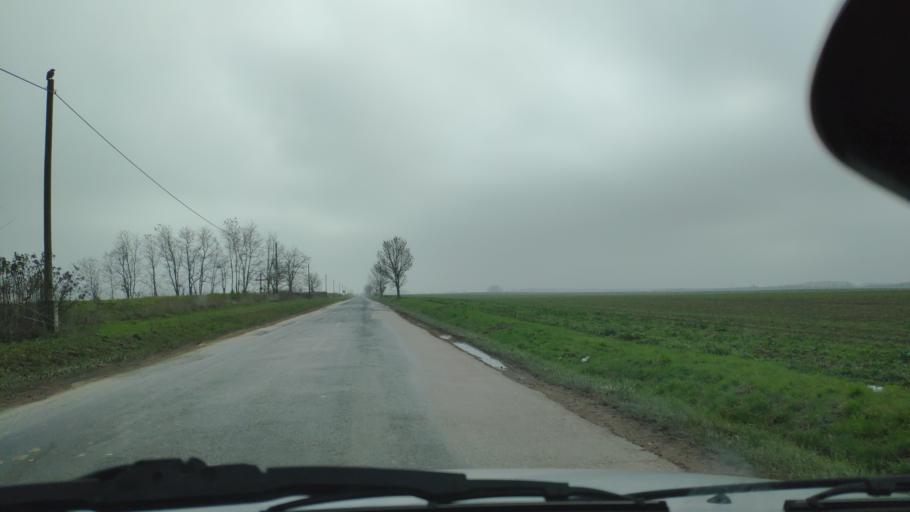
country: HU
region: Somogy
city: Balatonbereny
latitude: 46.6625
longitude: 17.2940
